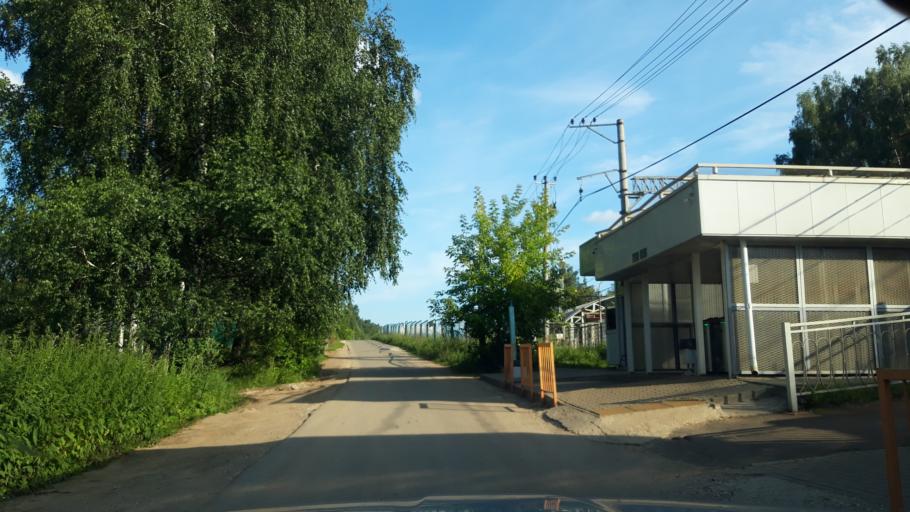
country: RU
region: Moskovskaya
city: Povarovo
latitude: 56.0647
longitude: 37.0762
